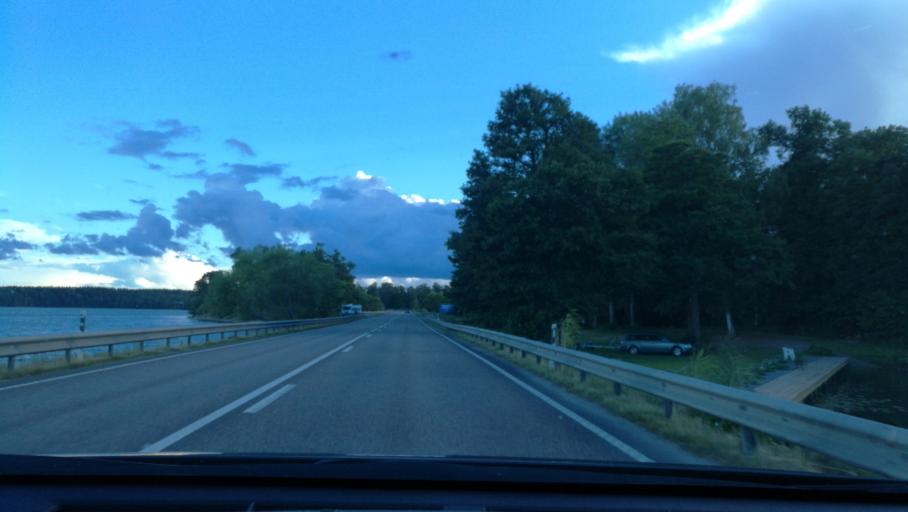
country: SE
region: Vaestmanland
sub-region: Kungsors Kommun
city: Kungsoer
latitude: 59.2496
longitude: 16.1075
